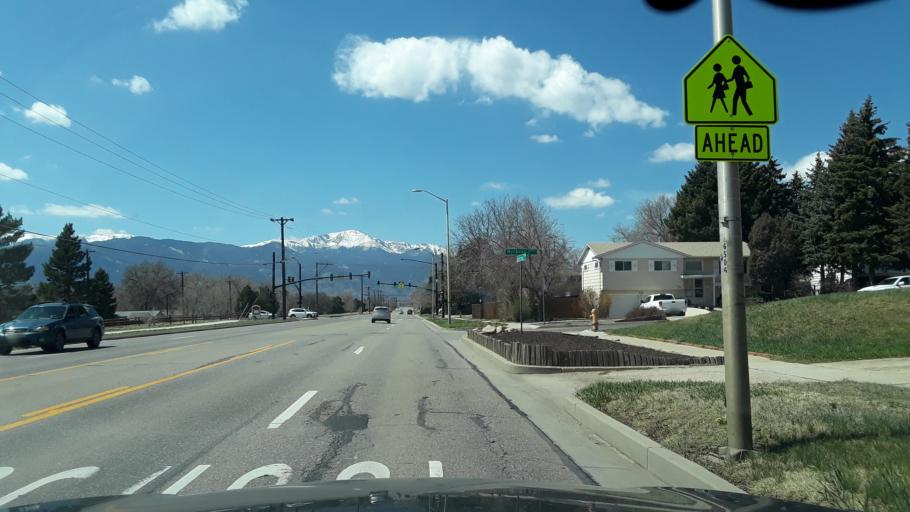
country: US
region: Colorado
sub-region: El Paso County
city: Colorado Springs
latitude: 38.8594
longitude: -104.7639
